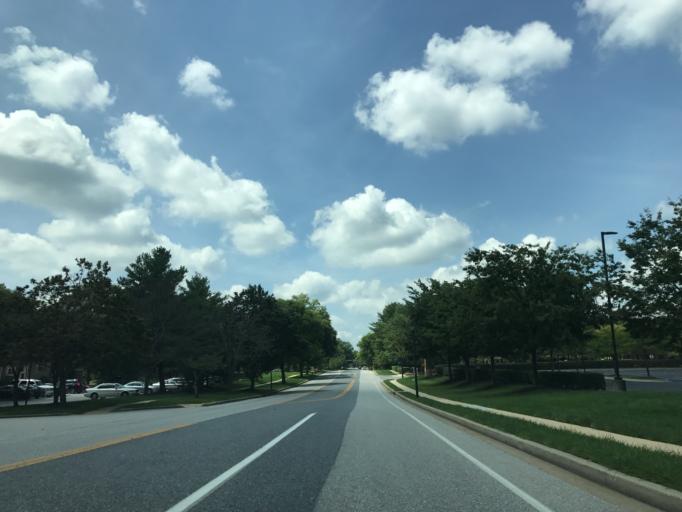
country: US
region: Maryland
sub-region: Howard County
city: Riverside
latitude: 39.2110
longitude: -76.8815
